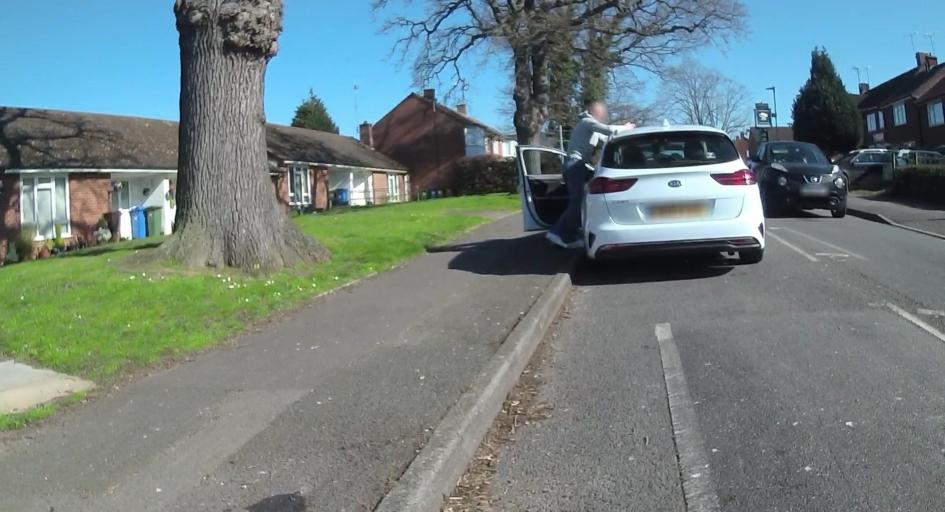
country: GB
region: England
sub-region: Bracknell Forest
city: Bracknell
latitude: 51.4237
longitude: -0.7559
